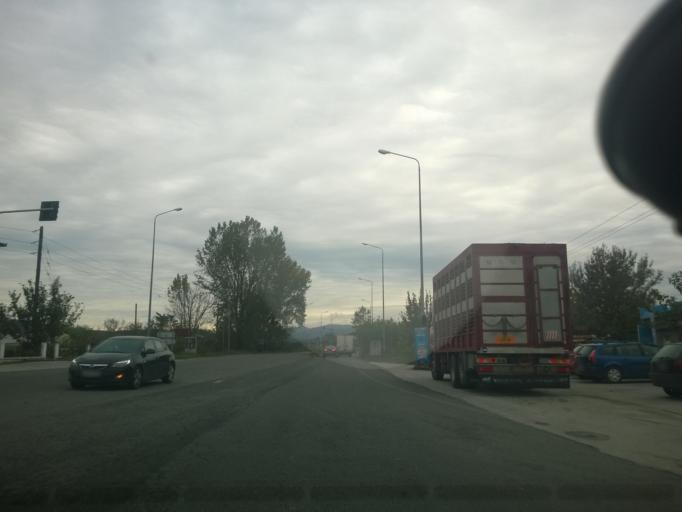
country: GR
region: Central Macedonia
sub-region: Nomos Pellis
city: Apsalos
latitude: 40.9283
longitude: 22.0839
